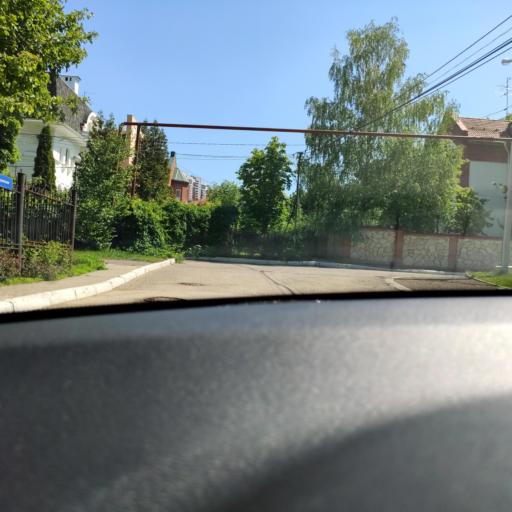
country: RU
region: Samara
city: Samara
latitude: 53.2403
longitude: 50.1747
